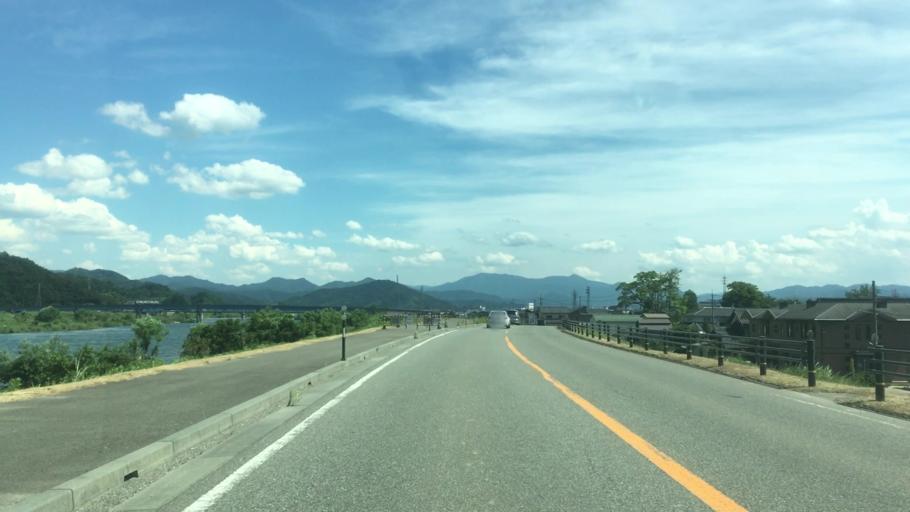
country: JP
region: Hyogo
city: Toyooka
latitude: 35.5616
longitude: 134.8138
